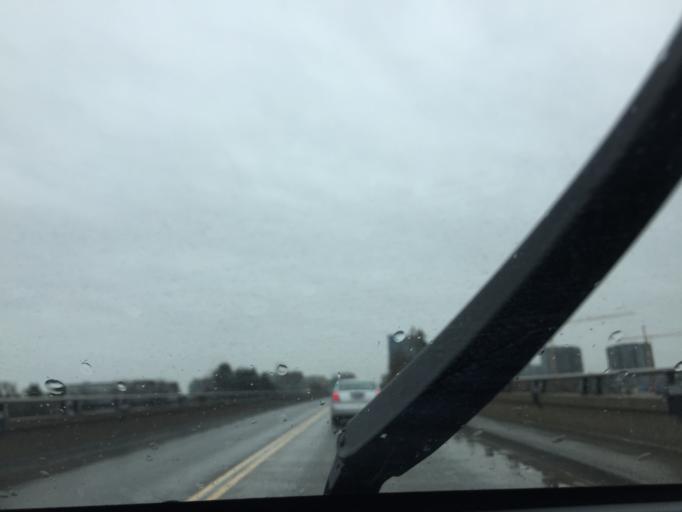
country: CA
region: British Columbia
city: Richmond
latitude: 49.1797
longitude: -123.1489
